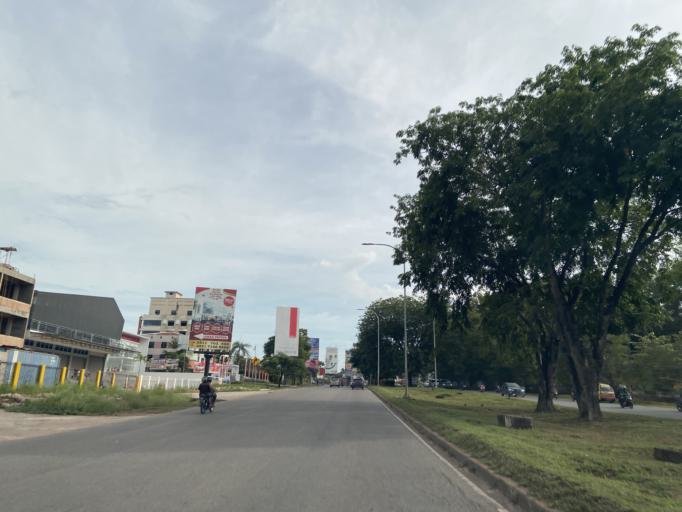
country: SG
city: Singapore
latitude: 1.1275
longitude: 104.0170
